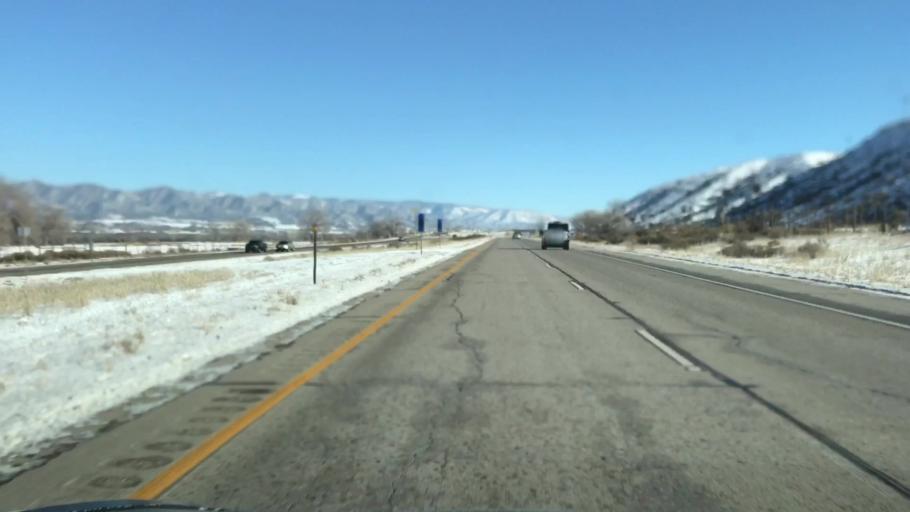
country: US
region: Colorado
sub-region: Garfield County
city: Rifle
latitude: 39.5306
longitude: -107.7230
